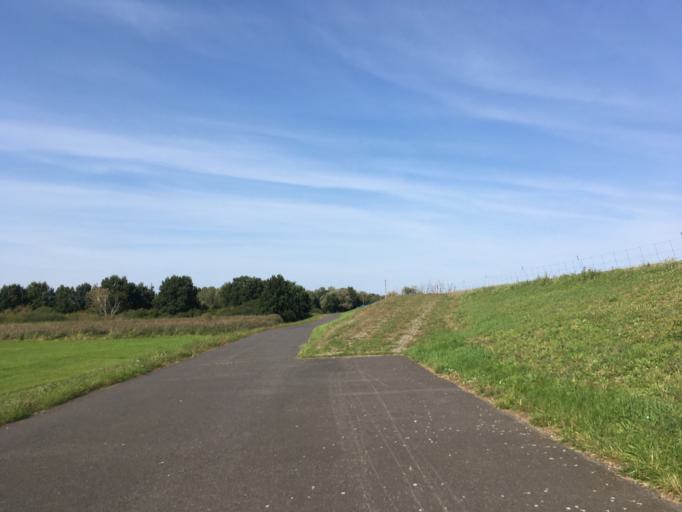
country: DE
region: Brandenburg
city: Vogelsang
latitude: 52.1920
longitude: 14.6828
